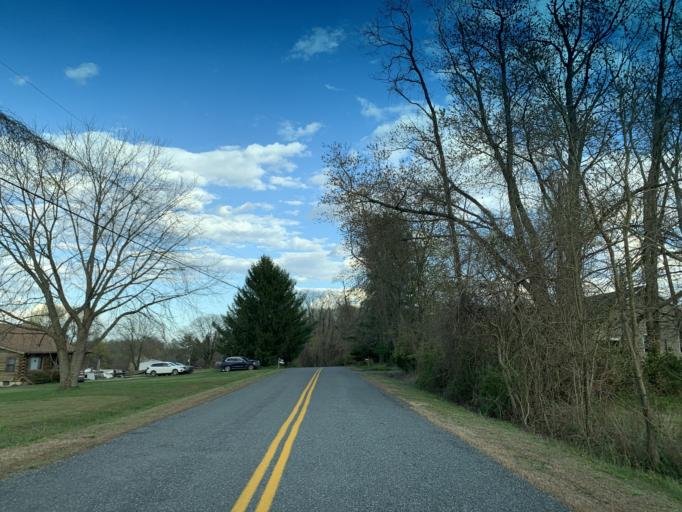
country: US
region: Maryland
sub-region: Harford County
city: South Bel Air
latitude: 39.5957
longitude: -76.3101
